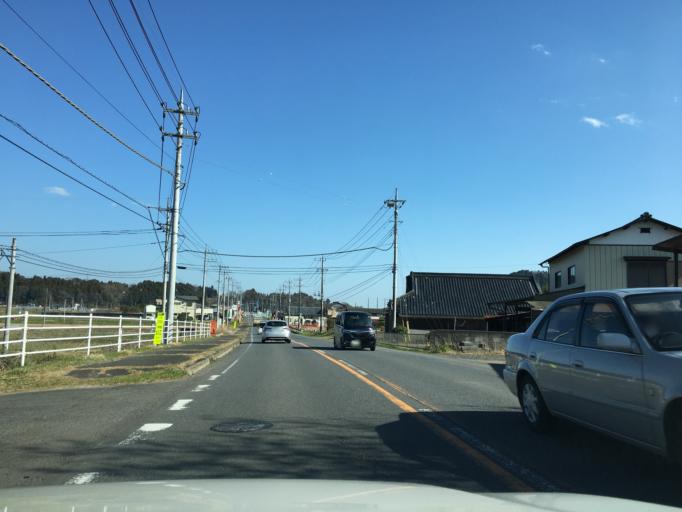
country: JP
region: Ibaraki
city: Omiya
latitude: 36.5592
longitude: 140.3107
